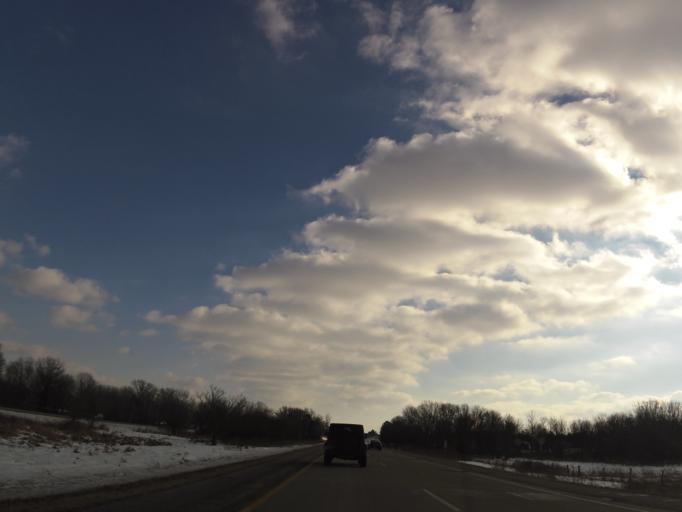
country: US
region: Wisconsin
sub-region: Juneau County
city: Mauston
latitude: 43.8506
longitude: -90.1048
